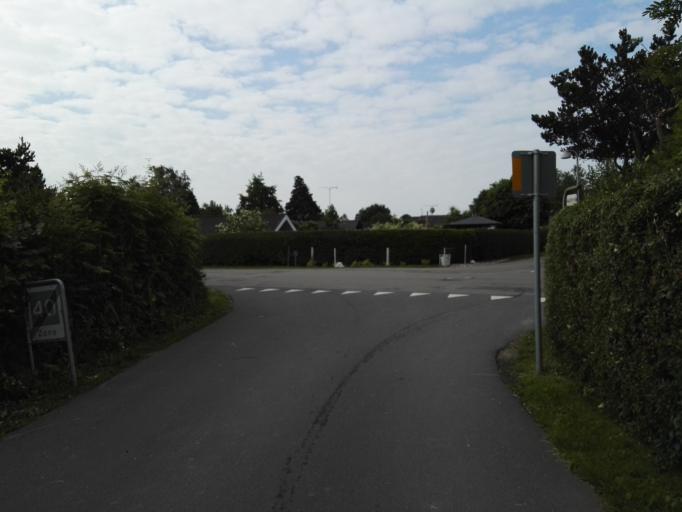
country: DK
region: Zealand
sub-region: Roskilde Kommune
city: Jyllinge
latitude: 55.7733
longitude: 12.0970
